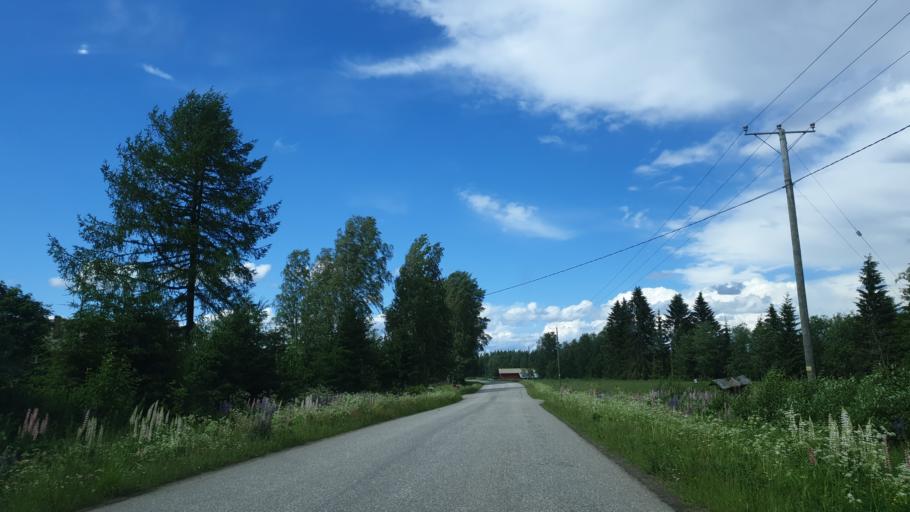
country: FI
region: Northern Savo
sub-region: Koillis-Savo
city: Kaavi
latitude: 62.9881
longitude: 28.7314
